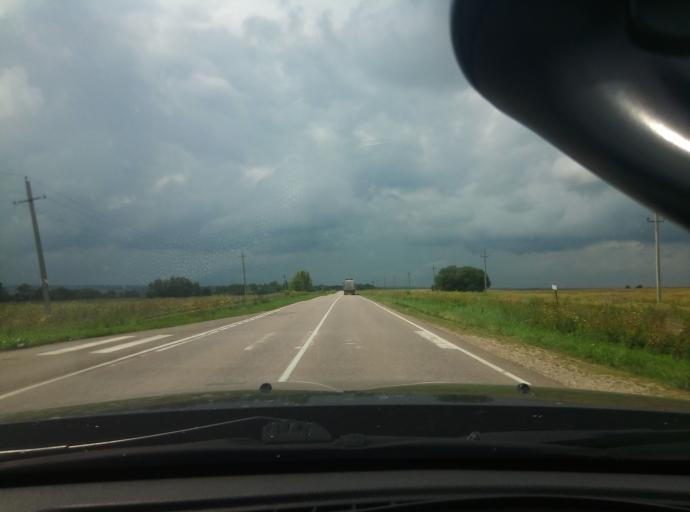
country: RU
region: Tula
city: Borodinskiy
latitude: 53.9834
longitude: 37.7714
